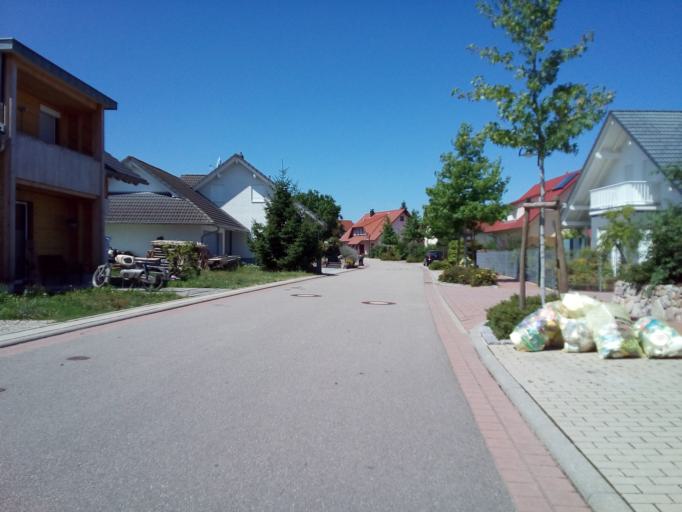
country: DE
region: Baden-Wuerttemberg
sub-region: Freiburg Region
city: Rheinau
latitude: 48.6555
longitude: 7.9267
